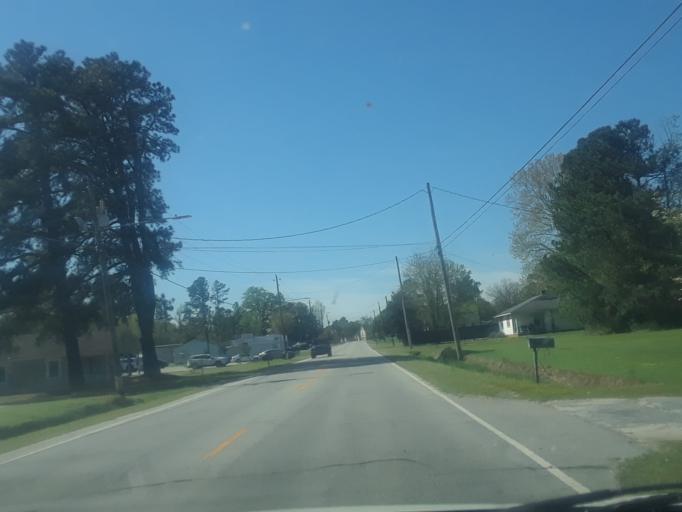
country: US
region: North Carolina
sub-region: Harnett County
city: Erwin
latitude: 35.3206
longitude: -78.6562
